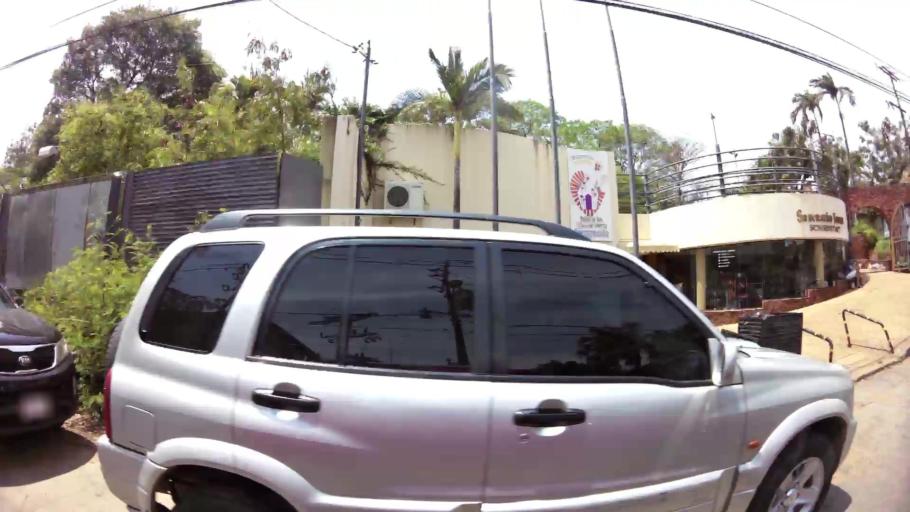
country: PY
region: Central
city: Lambare
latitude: -25.2966
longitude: -57.5751
